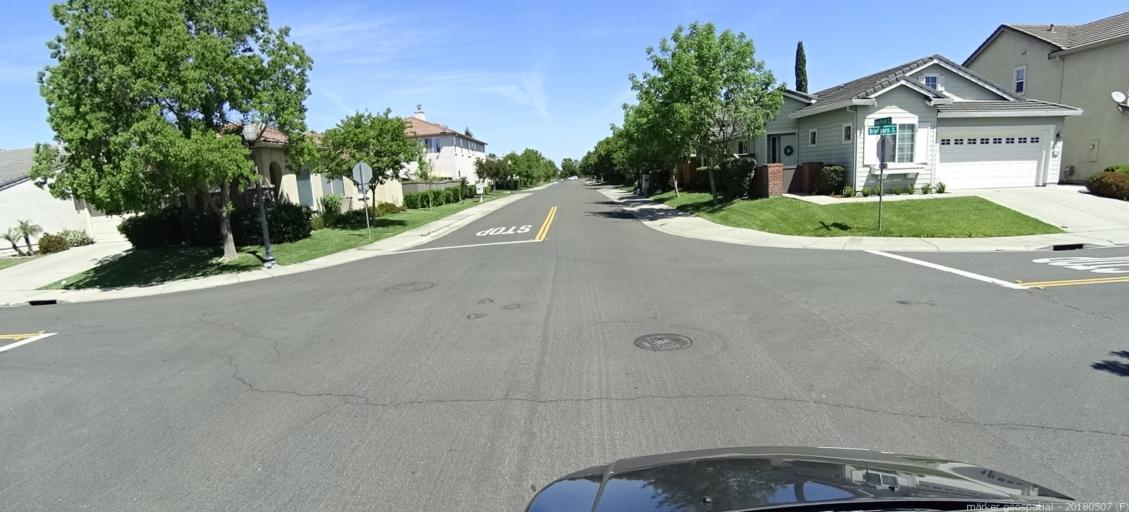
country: US
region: California
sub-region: Sacramento County
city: Elverta
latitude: 38.6747
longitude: -121.5103
